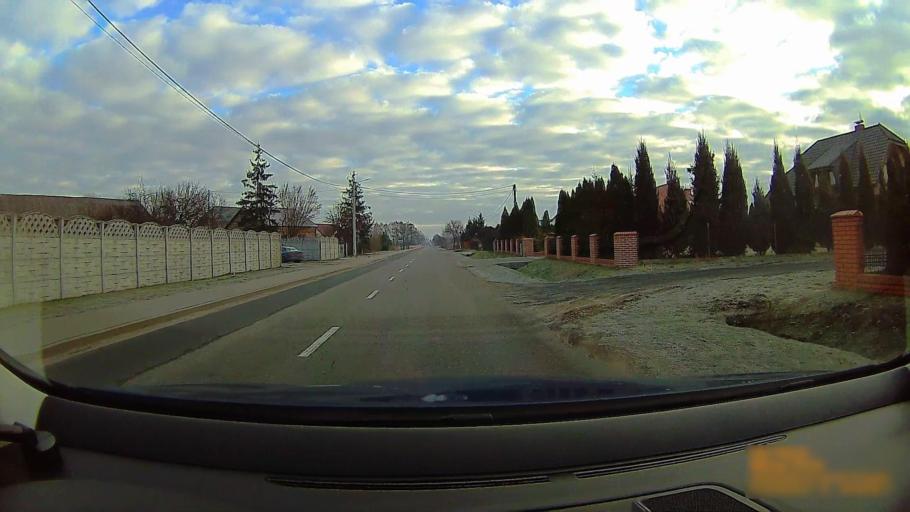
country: PL
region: Greater Poland Voivodeship
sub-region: Powiat koninski
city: Rzgow Pierwszy
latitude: 52.1577
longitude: 18.0575
